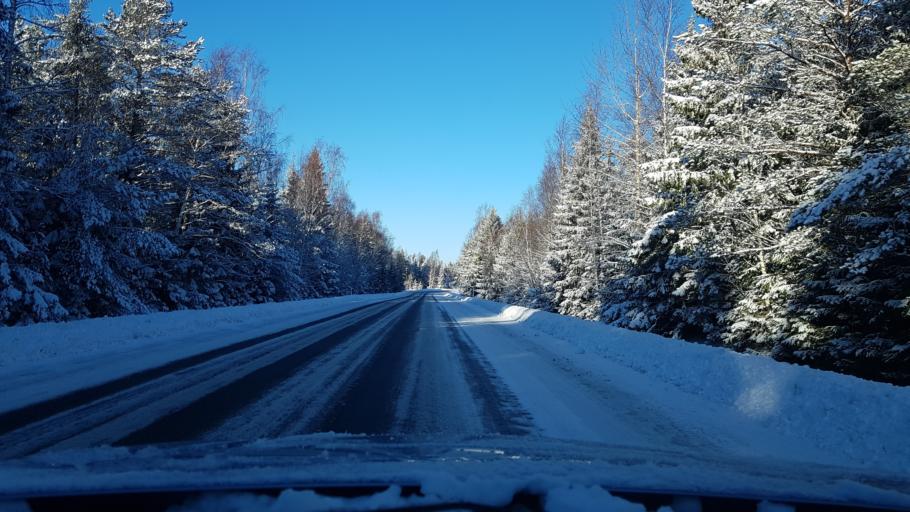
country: EE
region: Hiiumaa
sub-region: Kaerdla linn
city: Kardla
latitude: 58.9765
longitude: 22.8158
